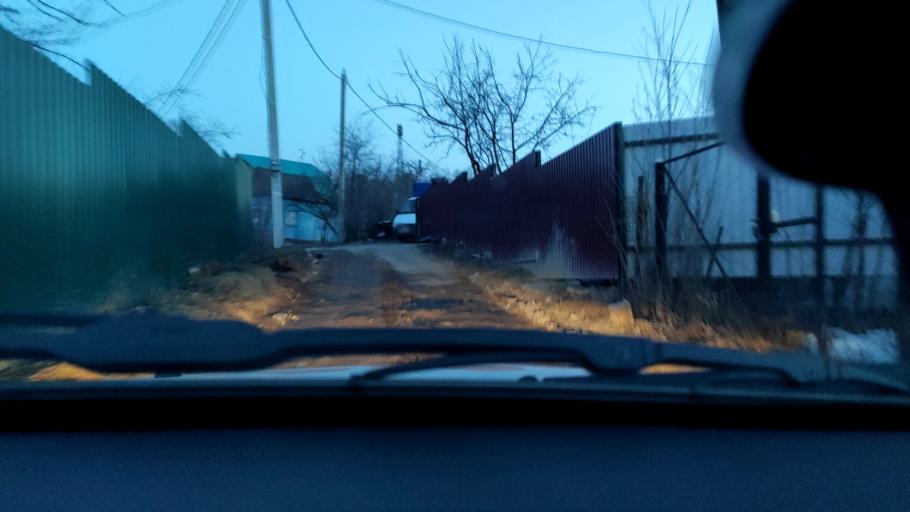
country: RU
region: Bashkortostan
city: Ufa
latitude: 54.8297
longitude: 56.0605
